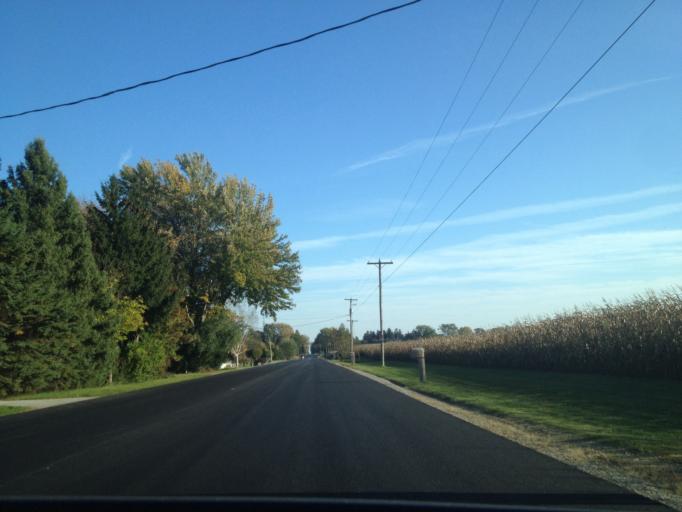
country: CA
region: Ontario
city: Delaware
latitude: 42.5724
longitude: -81.5682
